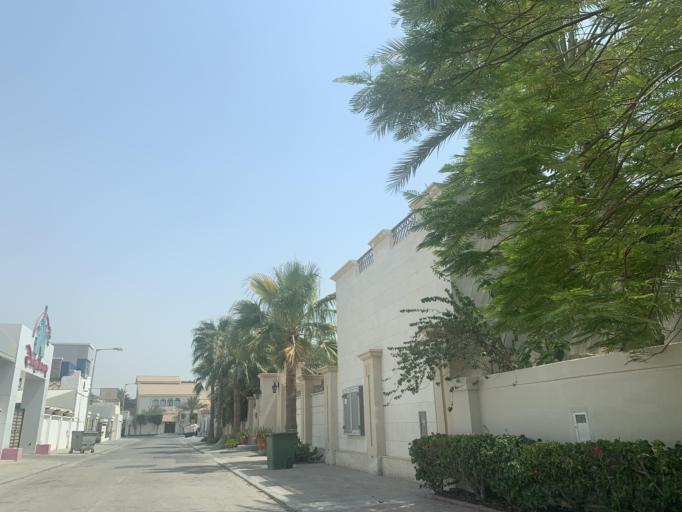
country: BH
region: Manama
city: Jidd Hafs
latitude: 26.1980
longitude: 50.4929
